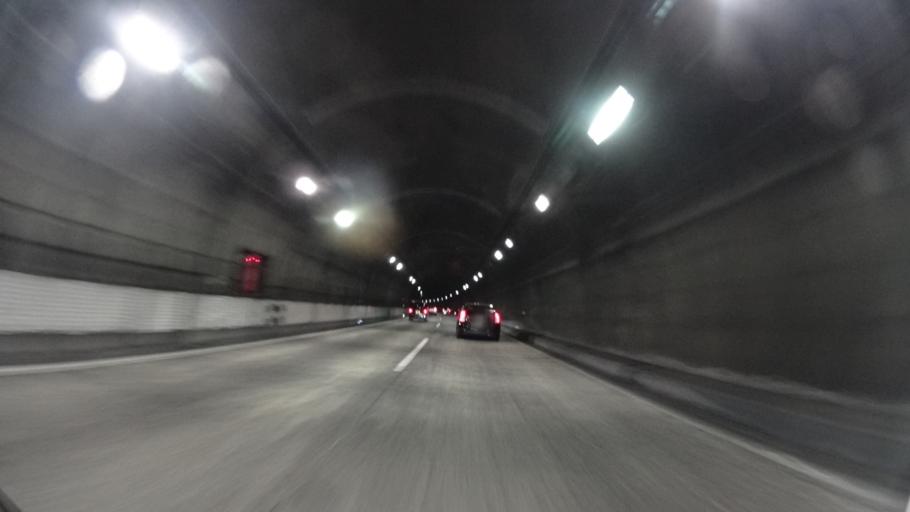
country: JP
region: Okayama
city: Okayama-shi
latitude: 34.7720
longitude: 134.1028
